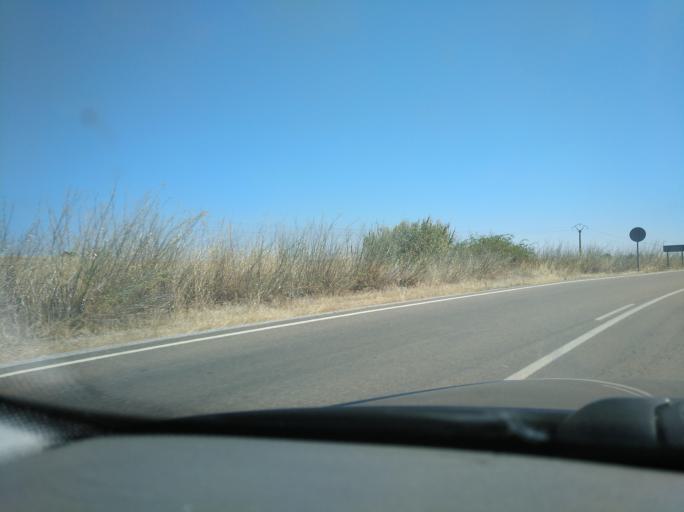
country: ES
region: Extremadura
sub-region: Provincia de Badajoz
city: Olivenza
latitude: 38.6972
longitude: -7.1347
